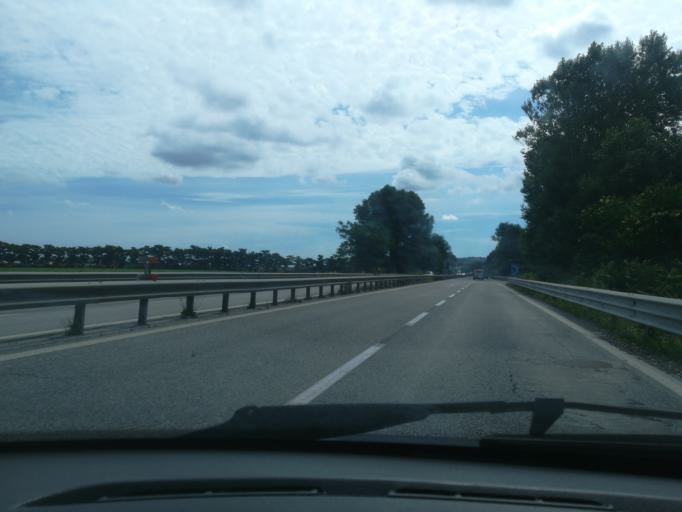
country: IT
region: The Marches
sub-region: Provincia di Macerata
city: Villa San Filippo
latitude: 43.2639
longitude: 13.5533
